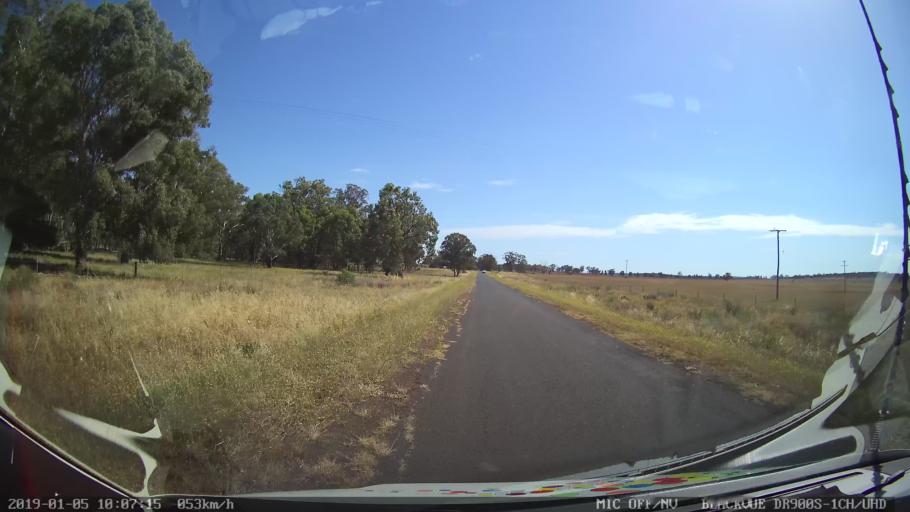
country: AU
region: New South Wales
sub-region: Gilgandra
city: Gilgandra
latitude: -31.6509
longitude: 148.8738
